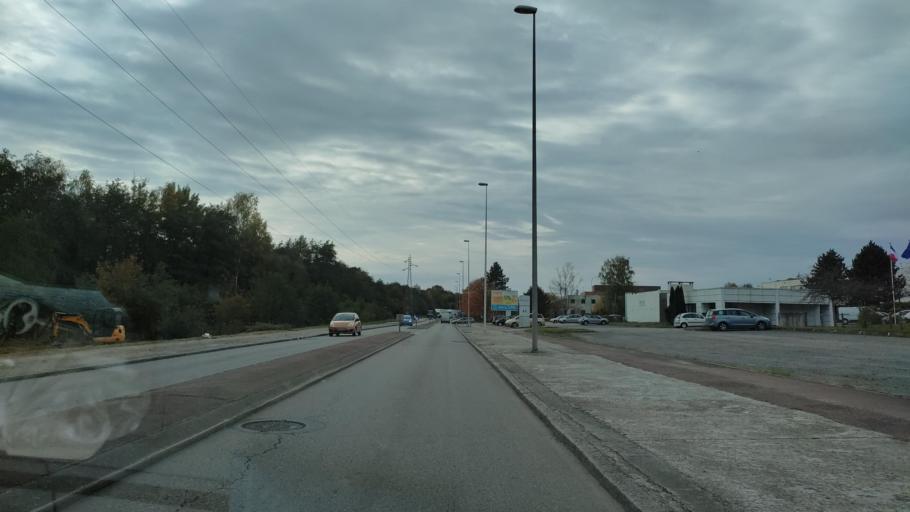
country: FR
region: Limousin
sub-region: Departement de la Haute-Vienne
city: Chaptelat
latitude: 45.8814
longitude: 1.2792
